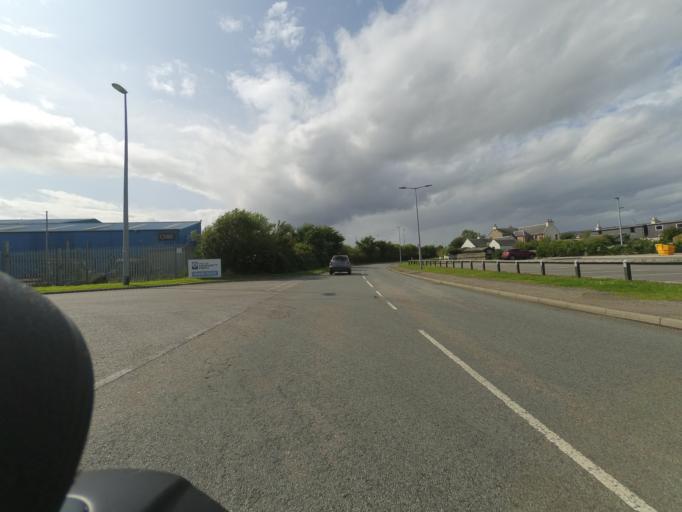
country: GB
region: Scotland
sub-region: Highland
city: Invergordon
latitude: 57.6871
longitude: -4.1741
